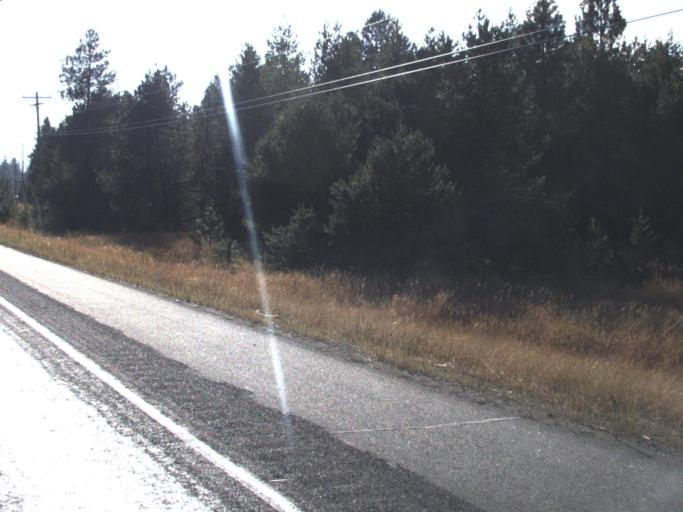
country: US
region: Washington
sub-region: Pend Oreille County
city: Newport
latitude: 48.1149
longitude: -117.2157
